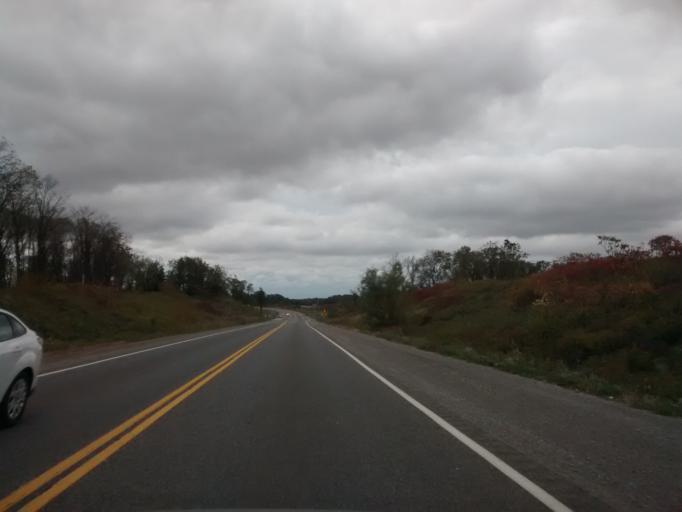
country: CA
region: Ontario
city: Ancaster
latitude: 43.1902
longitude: -79.9642
